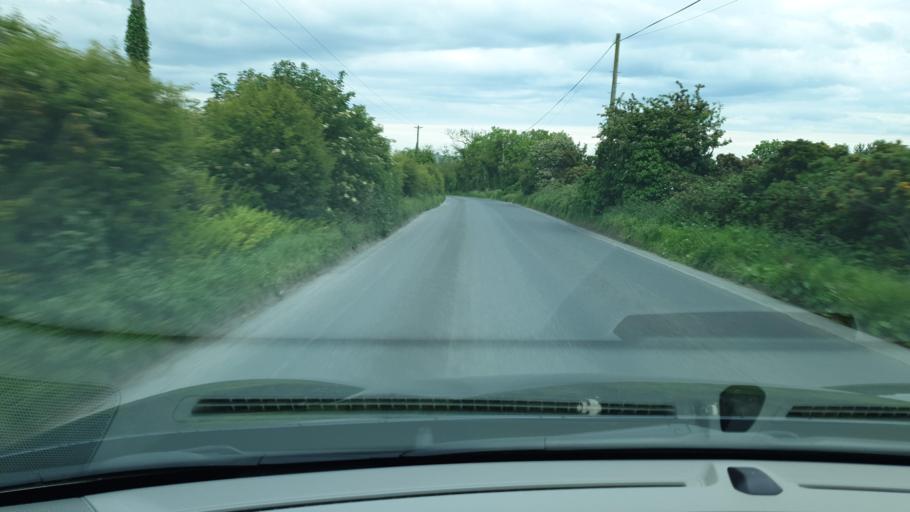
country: IE
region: Leinster
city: Balrothery
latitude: 53.5557
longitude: -6.2535
